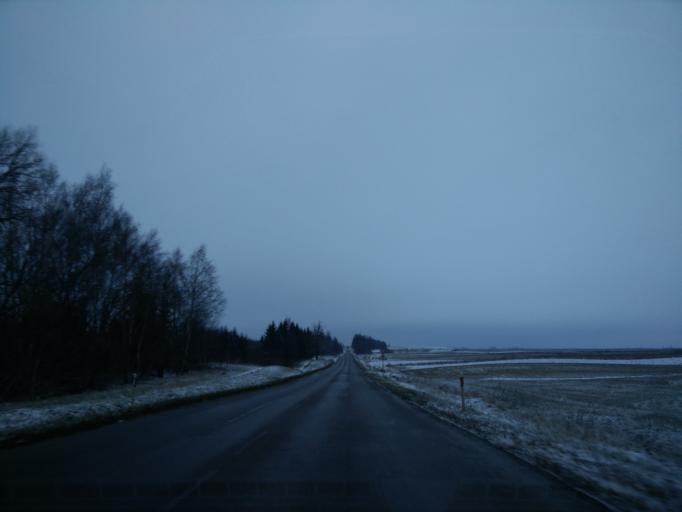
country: LT
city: Kelme
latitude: 55.6152
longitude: 22.9056
